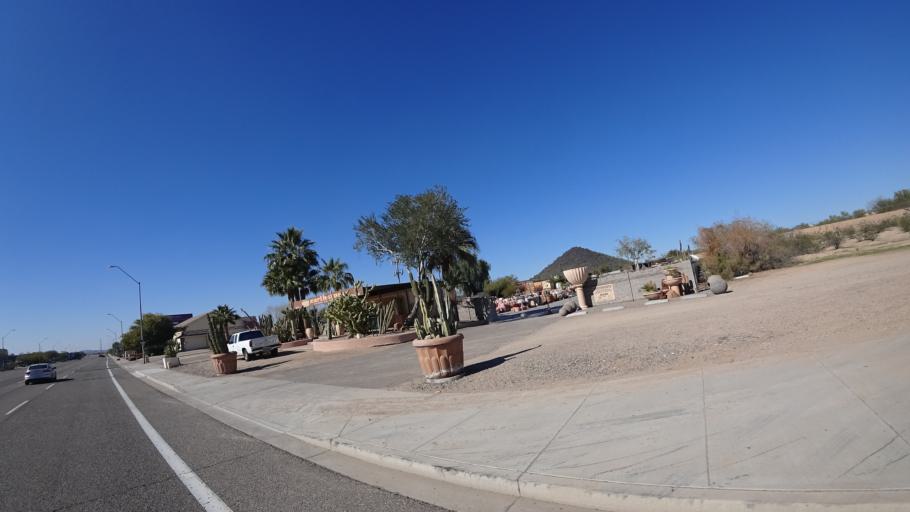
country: US
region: Arizona
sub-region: Maricopa County
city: Cave Creek
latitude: 33.6877
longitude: -112.0396
